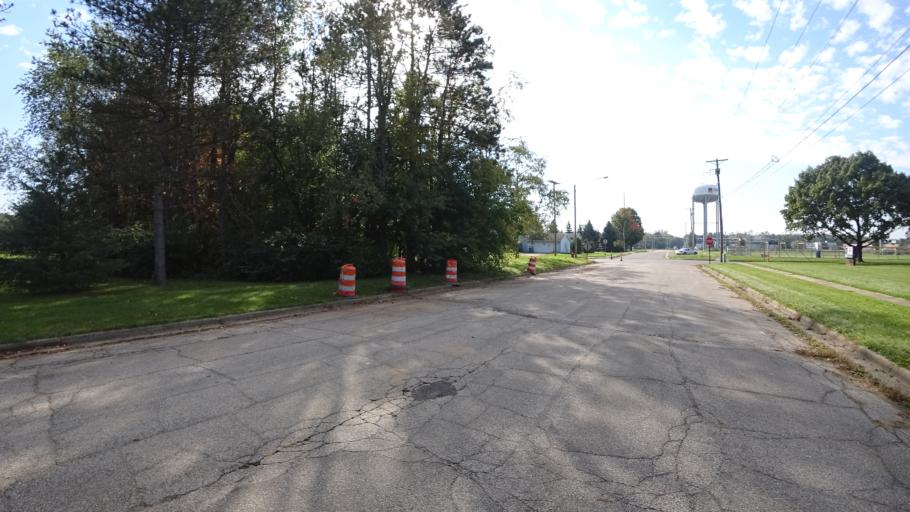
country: US
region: Michigan
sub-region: Saint Joseph County
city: Three Rivers
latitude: 41.9355
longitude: -85.6442
